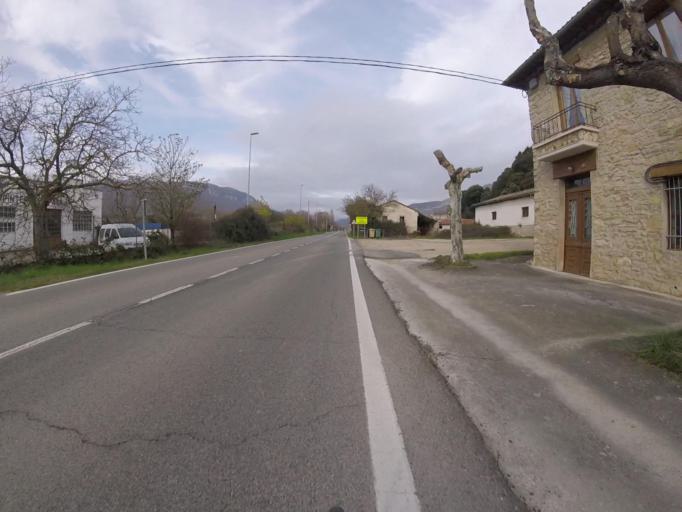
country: ES
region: Navarre
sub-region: Provincia de Navarra
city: Estella
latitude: 42.7120
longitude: -2.0721
